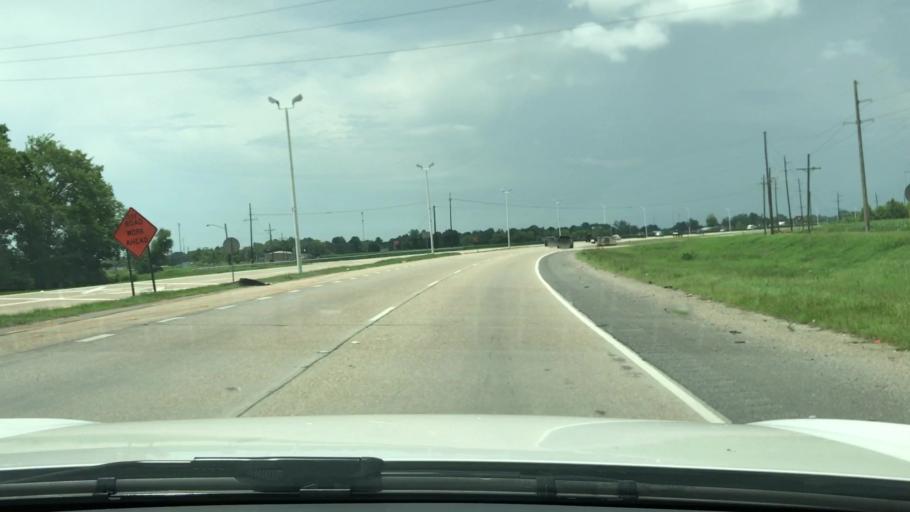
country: US
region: Louisiana
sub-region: West Baton Rouge Parish
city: Addis
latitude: 30.3409
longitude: -91.2611
